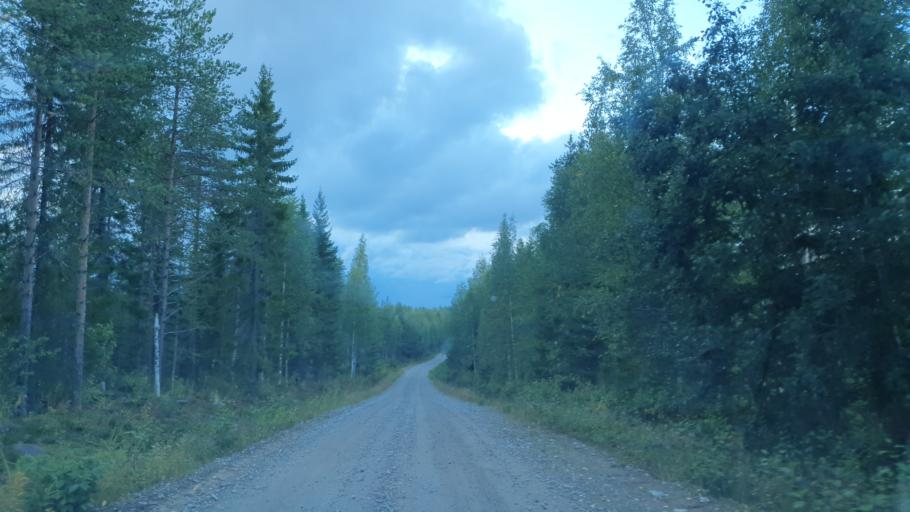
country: FI
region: Kainuu
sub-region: Kehys-Kainuu
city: Kuhmo
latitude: 64.3365
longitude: 29.9011
